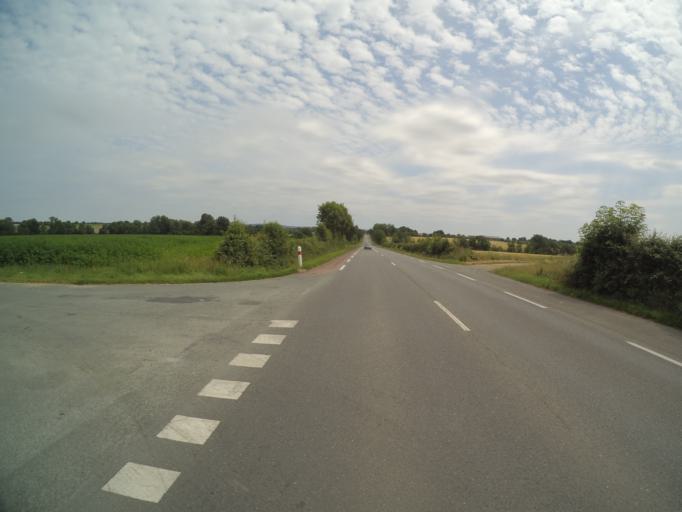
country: FR
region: Pays de la Loire
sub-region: Departement de la Vendee
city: Les Herbiers
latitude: 46.8468
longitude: -1.0693
